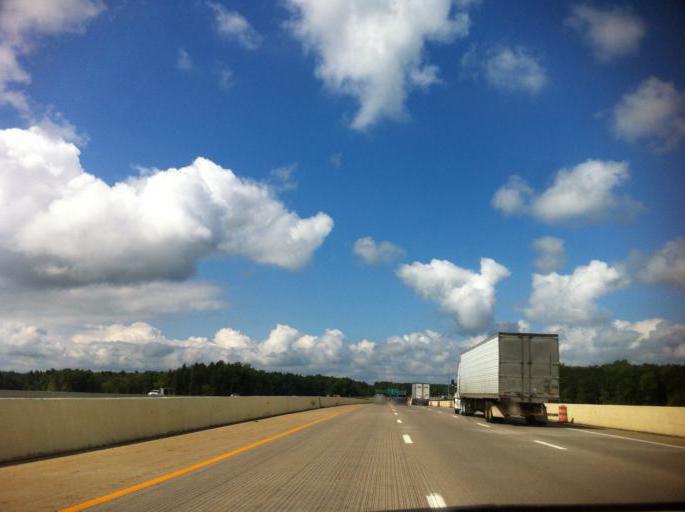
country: US
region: Ohio
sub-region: Mahoning County
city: Austintown
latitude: 41.1144
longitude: -80.8095
